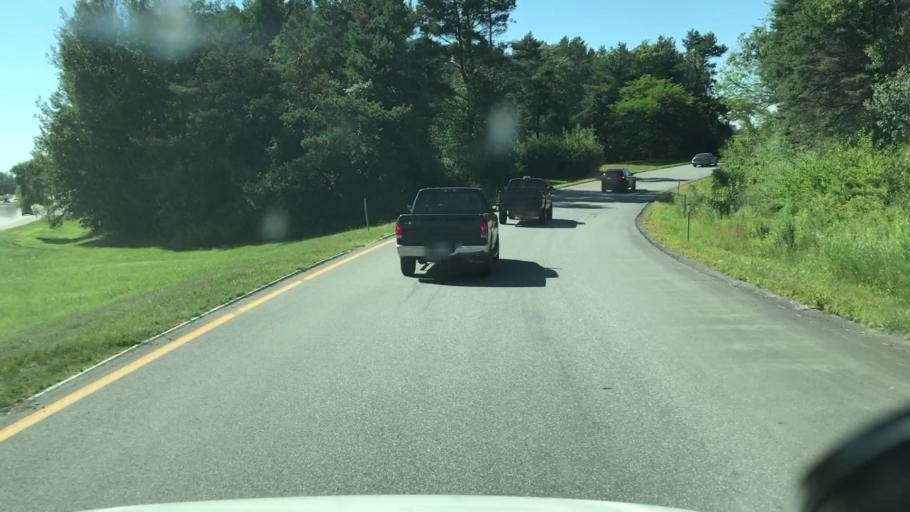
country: US
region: Maine
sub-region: Penobscot County
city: Bangor
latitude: 44.7868
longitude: -68.8042
